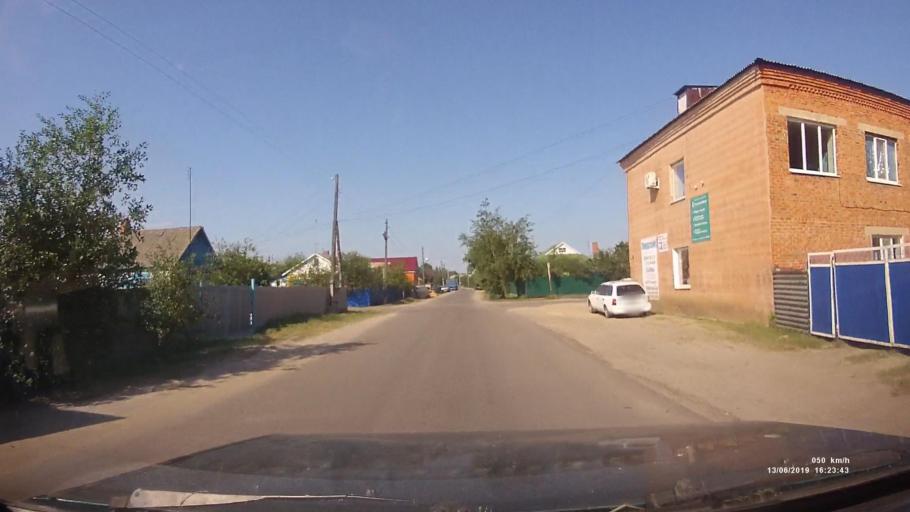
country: RU
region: Rostov
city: Kazanskaya
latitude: 49.7953
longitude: 41.1423
